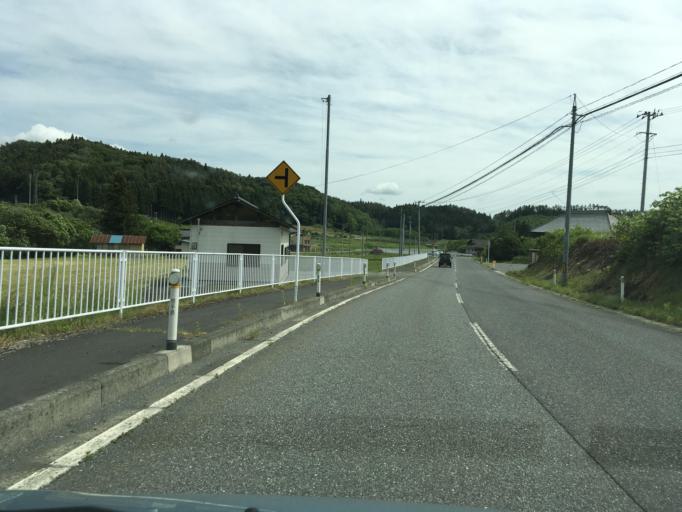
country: JP
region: Iwate
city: Mizusawa
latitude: 39.0823
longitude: 141.3535
